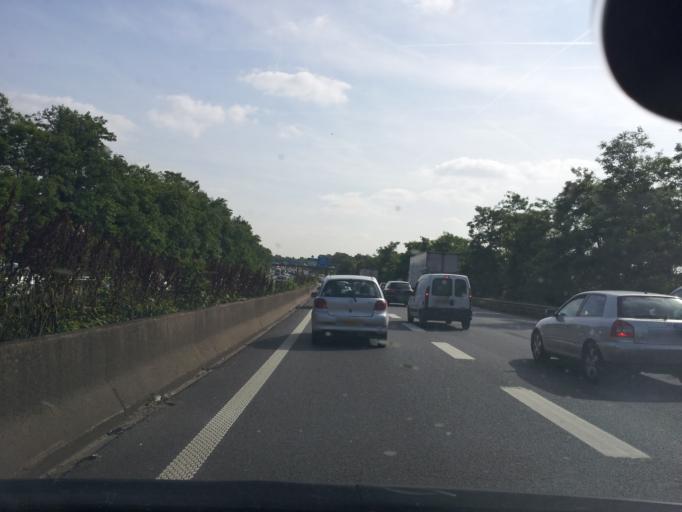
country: FR
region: Ile-de-France
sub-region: Departement de l'Essonne
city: Massy
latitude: 48.7212
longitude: 2.2951
